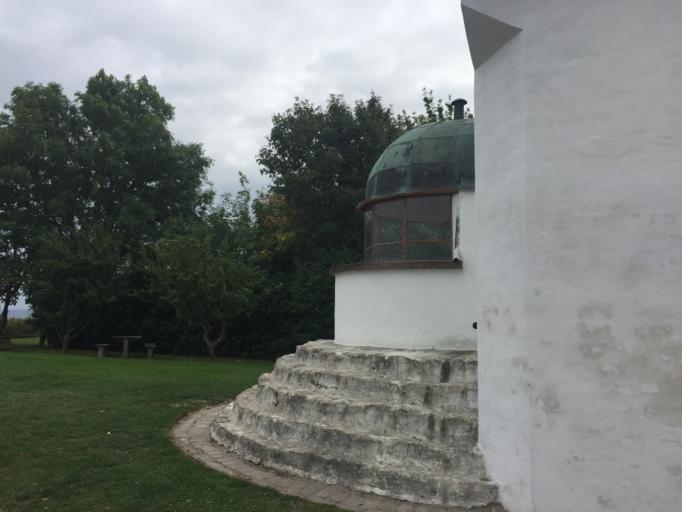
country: DK
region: Zealand
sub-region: Stevns Kommune
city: Store Heddinge
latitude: 55.2906
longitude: 12.4537
